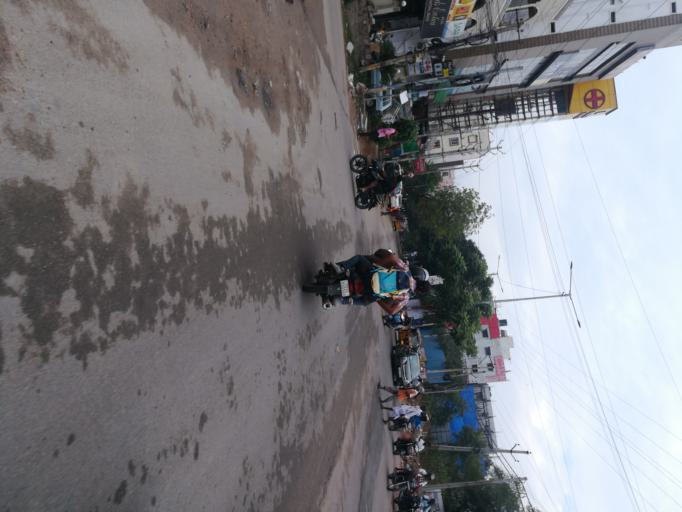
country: IN
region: Telangana
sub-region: Rangareddi
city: Kukatpalli
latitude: 17.4864
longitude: 78.3995
